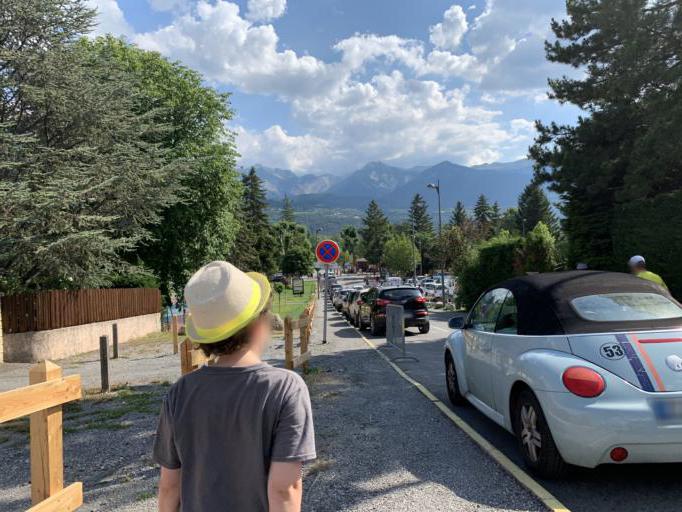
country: FR
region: Provence-Alpes-Cote d'Azur
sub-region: Departement des Hautes-Alpes
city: Embrun
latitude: 44.5517
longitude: 6.4795
